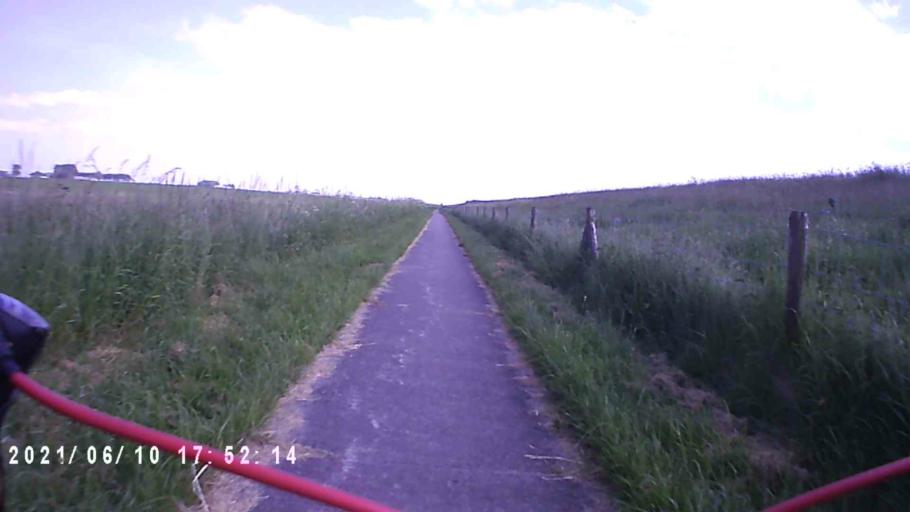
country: NL
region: Groningen
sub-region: Gemeente De Marne
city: Ulrum
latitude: 53.3289
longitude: 6.3172
